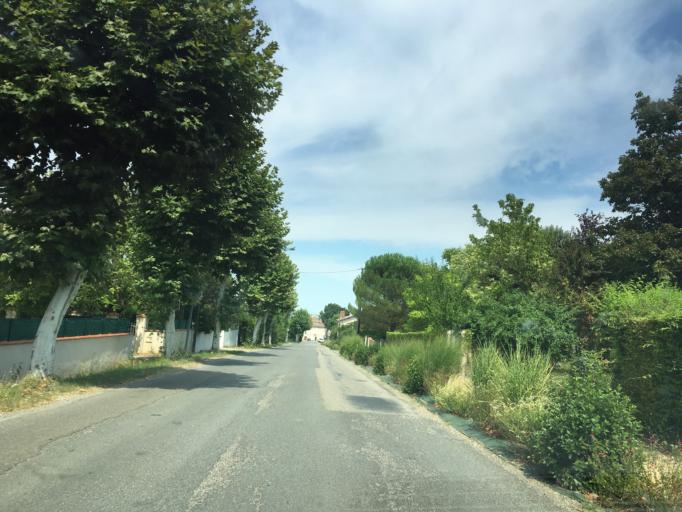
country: FR
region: Midi-Pyrenees
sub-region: Departement du Gers
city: Fleurance
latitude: 43.8874
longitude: 0.7652
